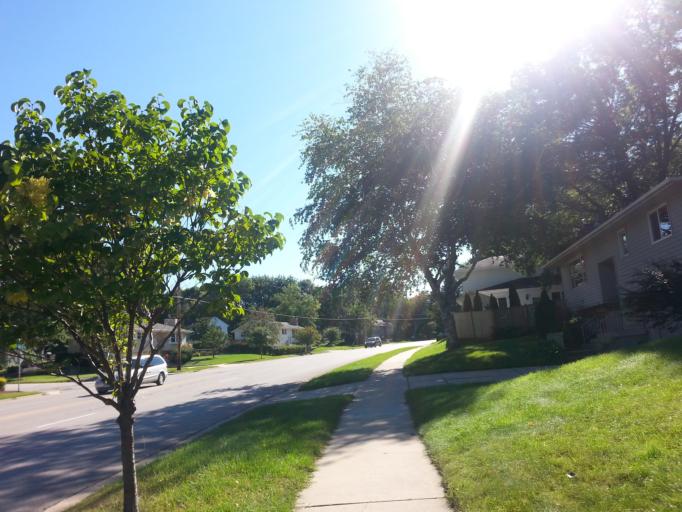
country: US
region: Minnesota
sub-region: Olmsted County
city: Rochester
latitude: 44.0498
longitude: -92.4747
